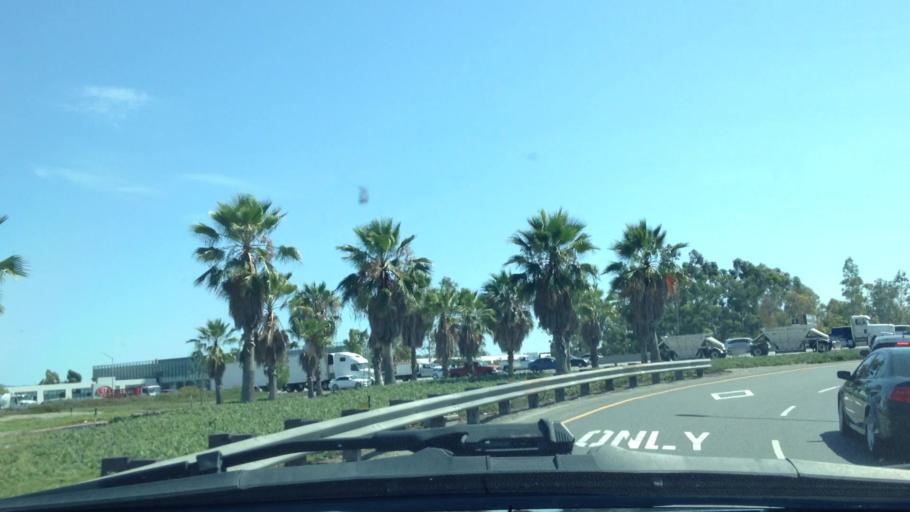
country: US
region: California
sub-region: Orange County
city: Tustin
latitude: 33.7198
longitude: -117.7935
